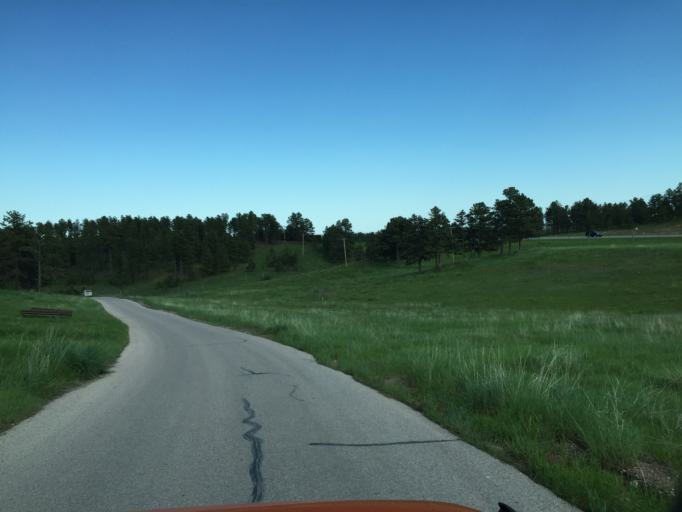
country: US
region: South Dakota
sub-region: Pennington County
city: Colonial Pine Hills
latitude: 43.9762
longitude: -103.2965
